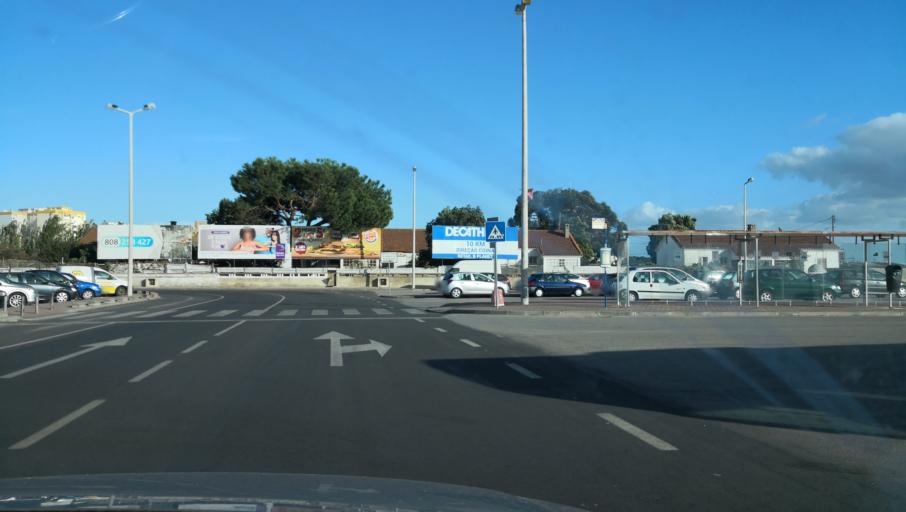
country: PT
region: Setubal
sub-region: Barreiro
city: Barreiro
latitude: 38.6524
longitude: -9.0774
